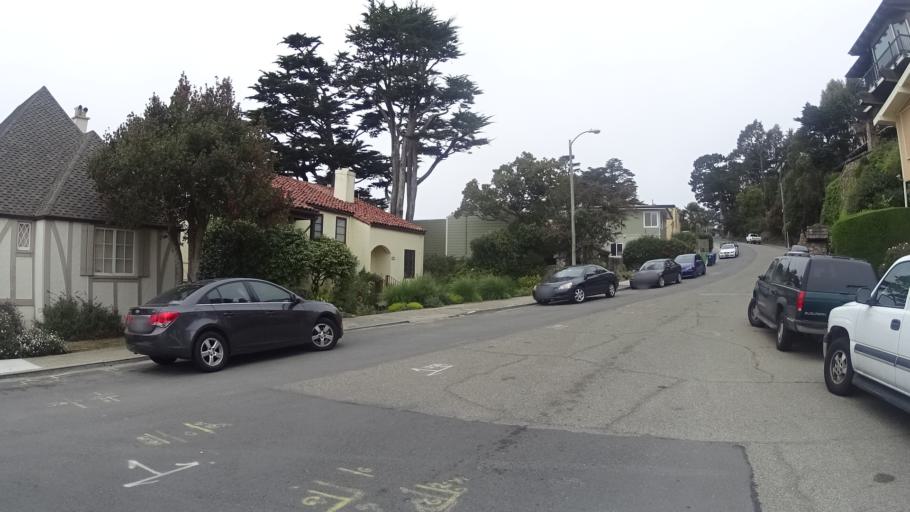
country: US
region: California
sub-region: San Mateo County
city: Daly City
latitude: 37.7356
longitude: -122.4598
